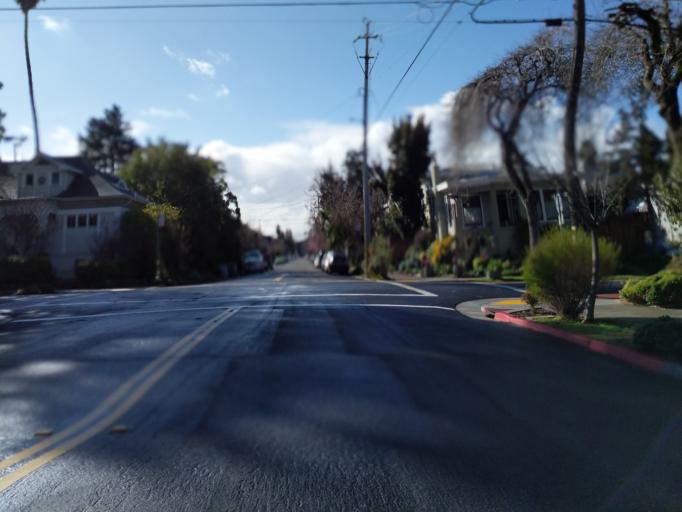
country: US
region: California
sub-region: Alameda County
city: Berkeley
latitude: 37.8612
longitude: -122.2762
